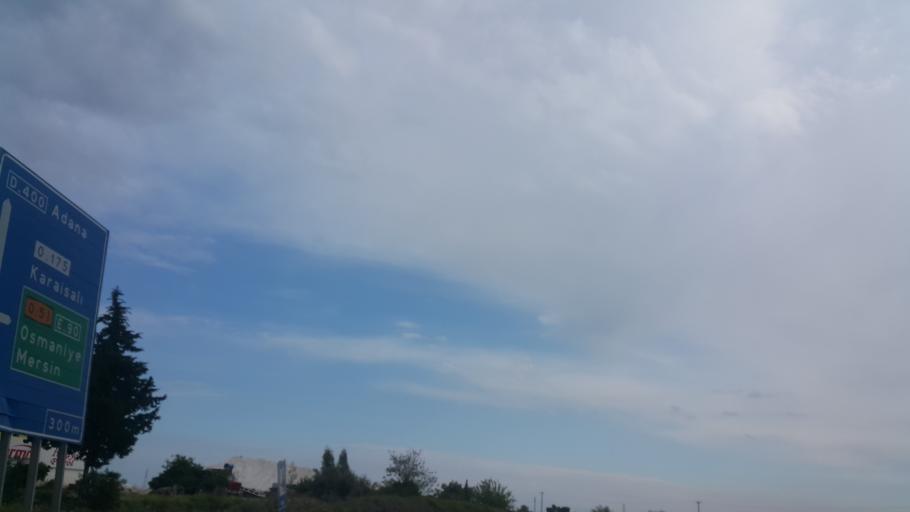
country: TR
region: Mersin
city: Yenice
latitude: 36.9917
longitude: 35.1759
